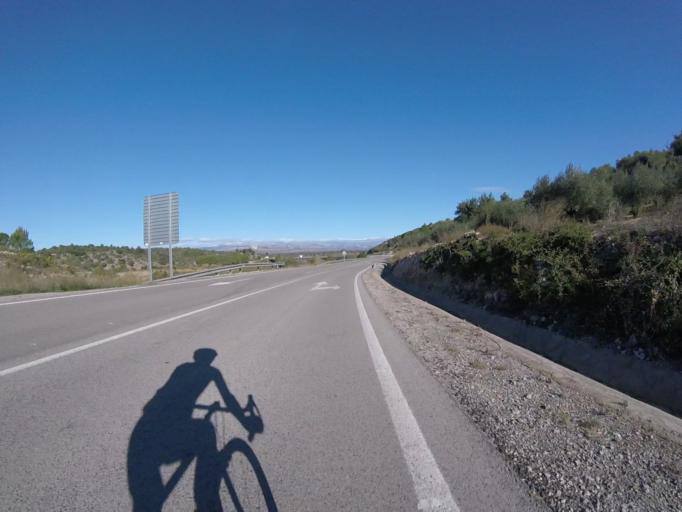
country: ES
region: Valencia
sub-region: Provincia de Castello
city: Cervera del Maestre
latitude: 40.4635
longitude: 0.2517
